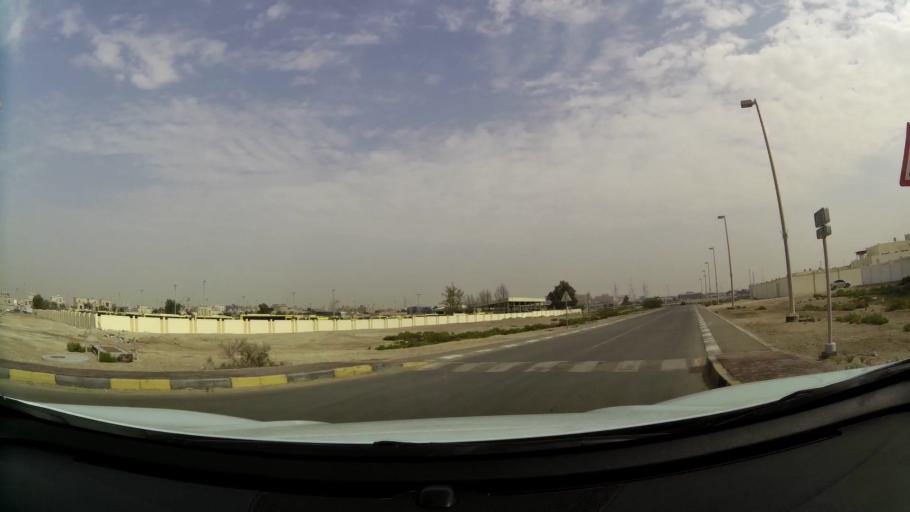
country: AE
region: Abu Dhabi
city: Abu Dhabi
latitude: 24.2865
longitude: 54.6569
